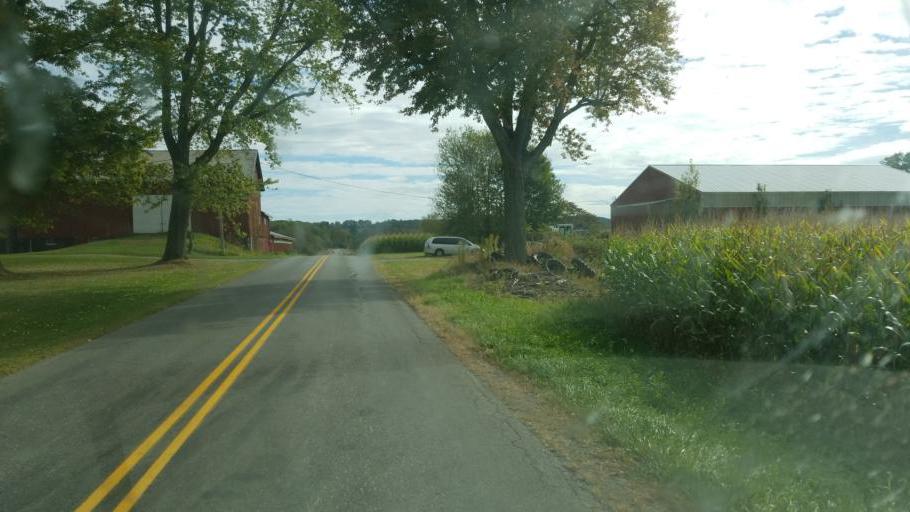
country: US
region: Pennsylvania
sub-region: Mercer County
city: Reynolds Heights
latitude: 41.3491
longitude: -80.2765
